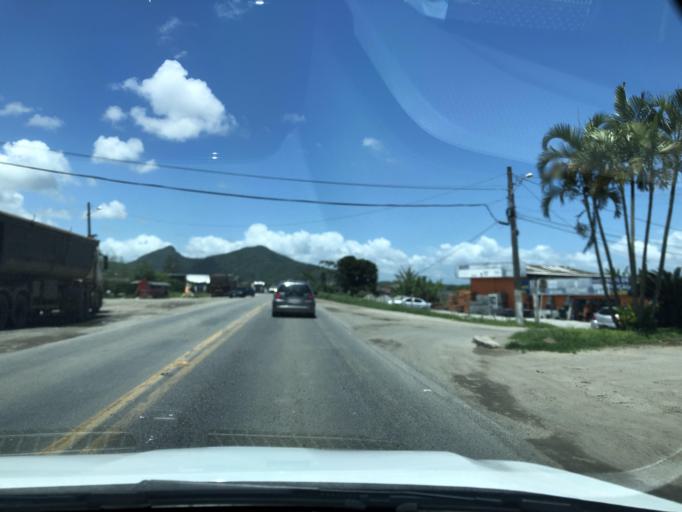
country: BR
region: Santa Catarina
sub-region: Sao Francisco Do Sul
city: Sao Francisco do Sul
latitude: -26.2675
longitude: -48.6361
